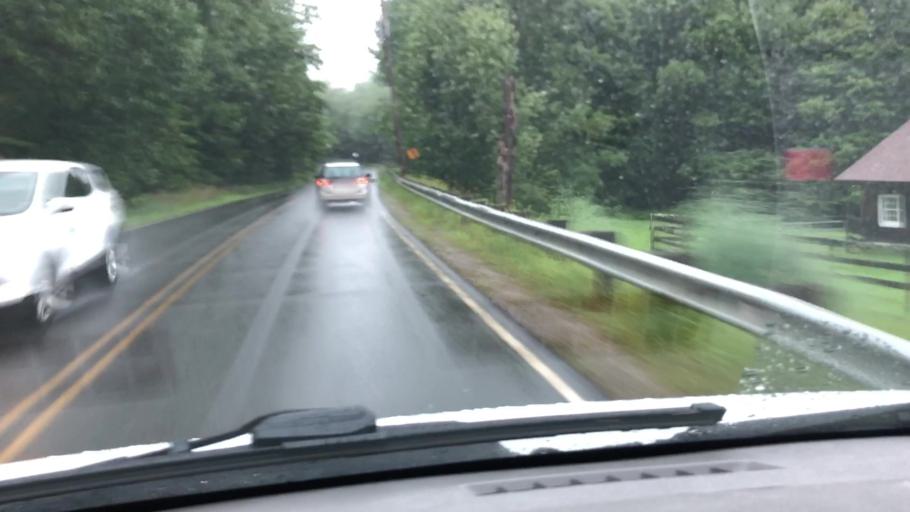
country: US
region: Massachusetts
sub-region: Hampshire County
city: Chesterfield
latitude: 42.4450
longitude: -72.9767
